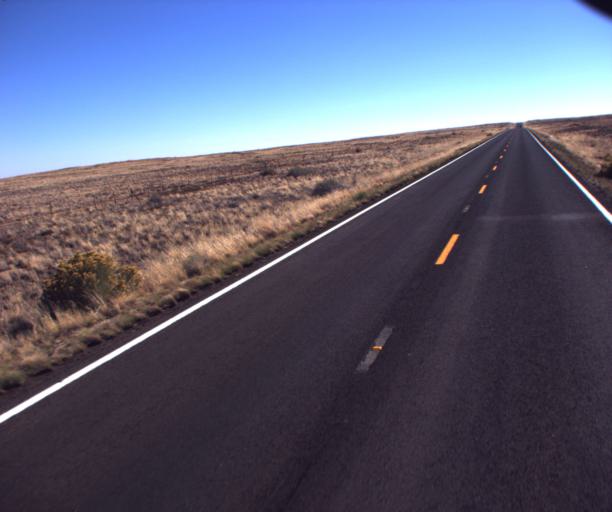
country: US
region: Arizona
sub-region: Coconino County
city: Tuba City
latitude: 35.9772
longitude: -110.9794
